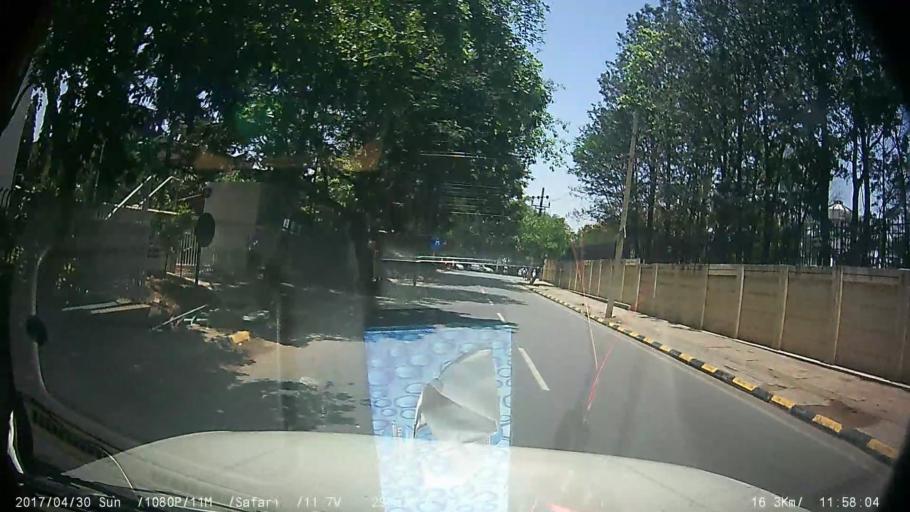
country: IN
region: Karnataka
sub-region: Bangalore Urban
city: Anekal
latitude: 12.8454
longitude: 77.6613
